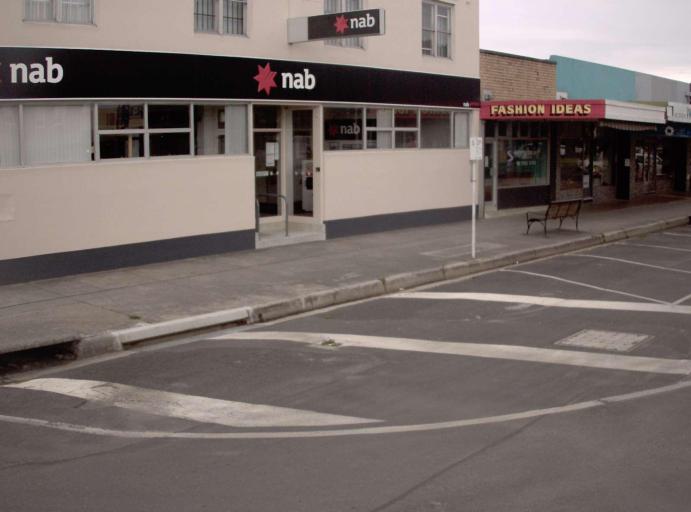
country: AU
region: Victoria
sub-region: Latrobe
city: Traralgon
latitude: -38.5624
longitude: 146.6762
